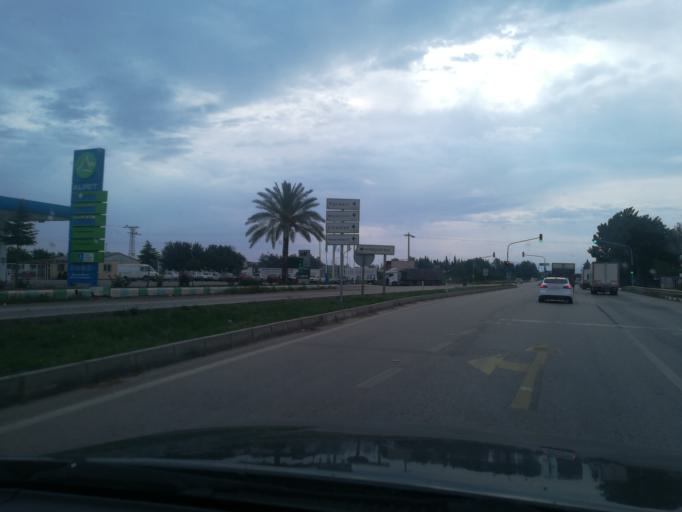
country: TR
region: Adana
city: Yakapinar
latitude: 36.9729
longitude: 35.5079
